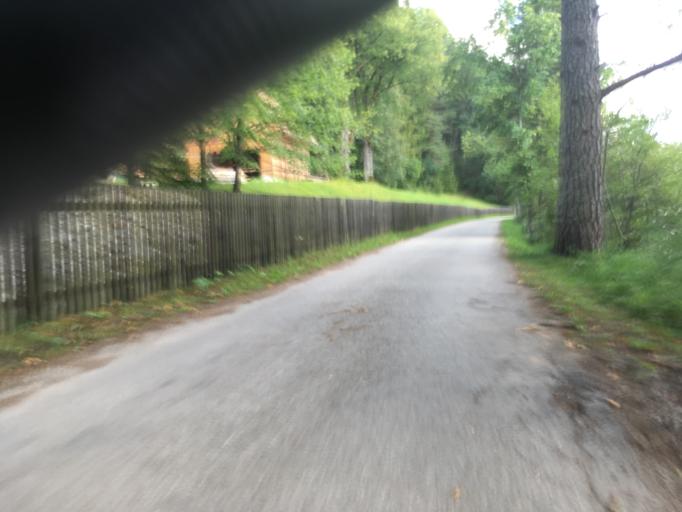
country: AT
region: Lower Austria
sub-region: Politischer Bezirk Lilienfeld
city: Mitterbach am Erlaufsee
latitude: 47.7950
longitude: 15.2720
